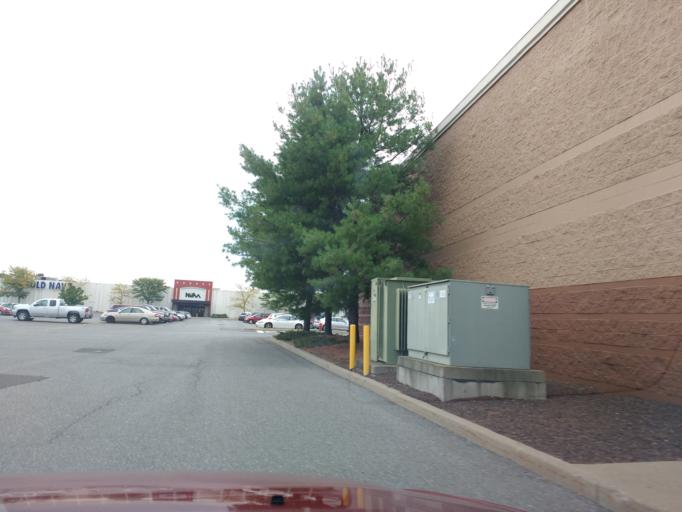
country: US
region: New York
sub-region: Ulster County
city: Lake Katrine
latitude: 41.9686
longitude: -73.9839
